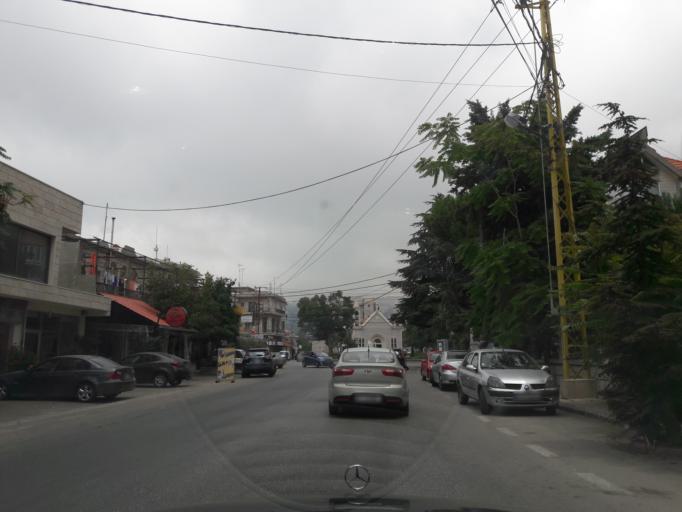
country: LB
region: Mont-Liban
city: Bhamdoun el Mhatta
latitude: 33.9123
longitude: 35.7482
